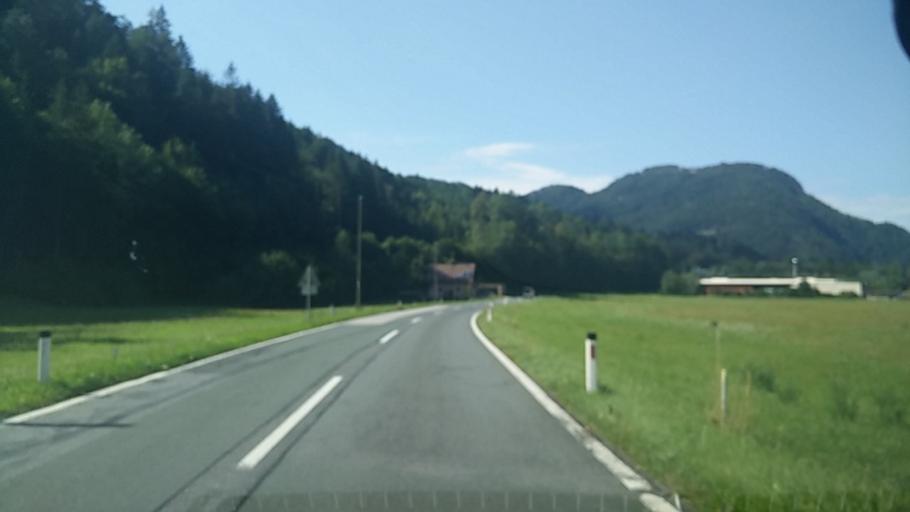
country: AT
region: Carinthia
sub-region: Politischer Bezirk Volkermarkt
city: Bad Eisenkappel
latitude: 46.5057
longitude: 14.5801
